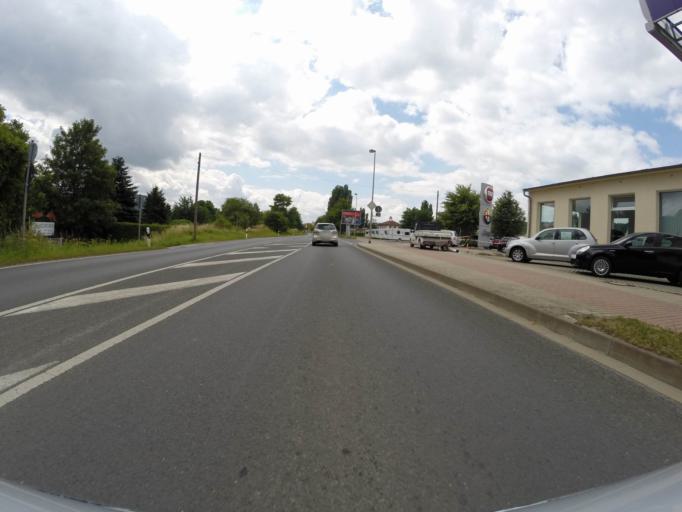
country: DE
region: Thuringia
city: Jena
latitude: 50.9410
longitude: 11.6035
